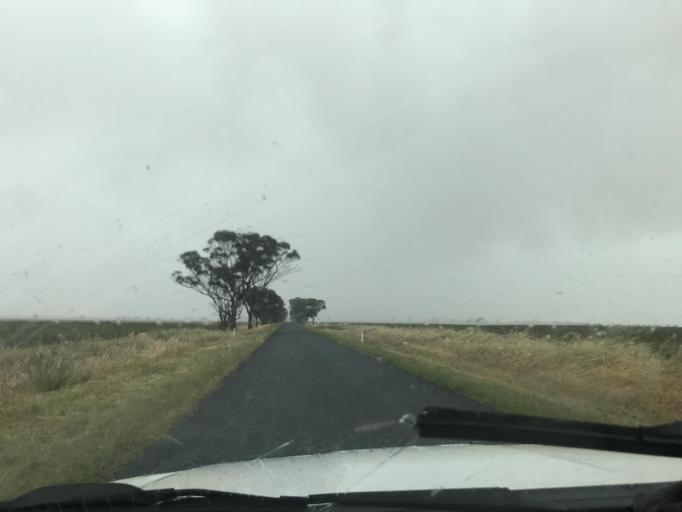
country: AU
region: South Australia
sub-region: Tatiara
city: Bordertown
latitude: -36.3152
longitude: 141.1651
